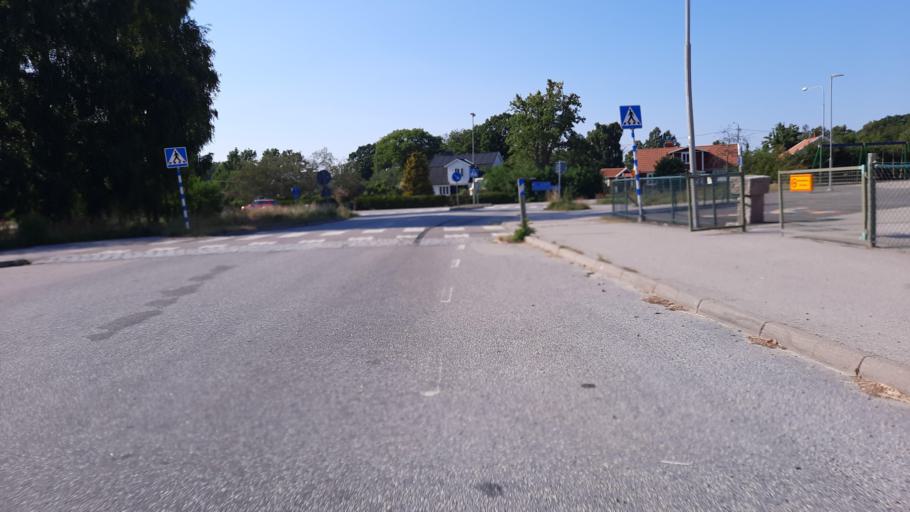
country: SE
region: Blekinge
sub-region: Karlskrona Kommun
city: Sturko
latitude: 56.1121
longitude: 15.6808
